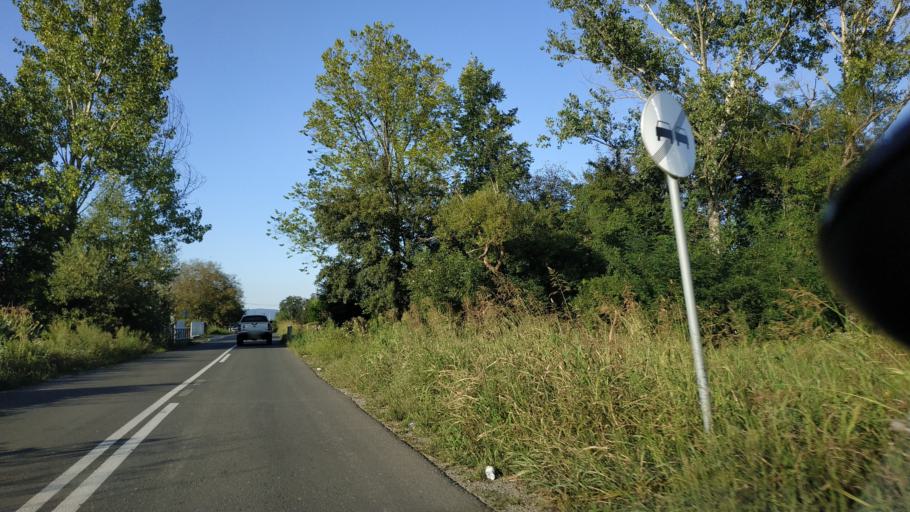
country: RS
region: Central Serbia
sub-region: Rasinski Okrug
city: Krusevac
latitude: 43.5301
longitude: 21.3409
